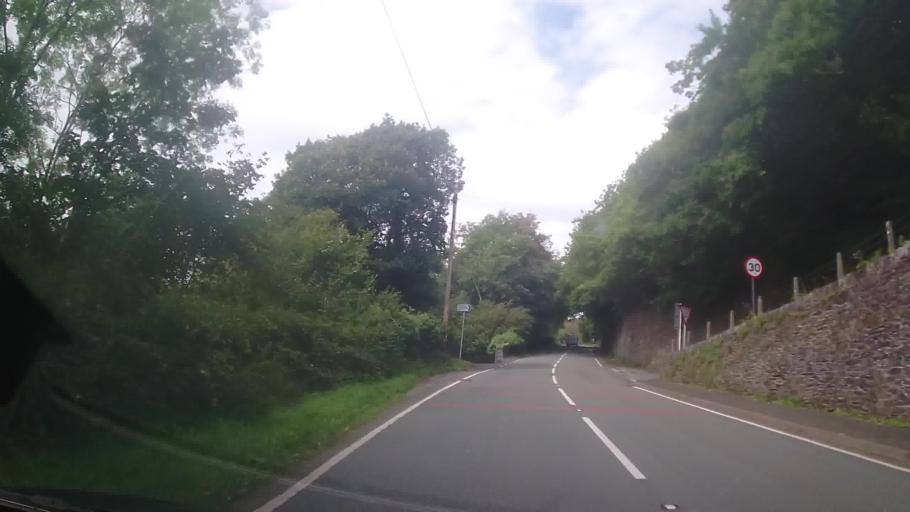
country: GB
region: Wales
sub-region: Gwynedd
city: Barmouth
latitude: 52.7149
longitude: -4.0038
